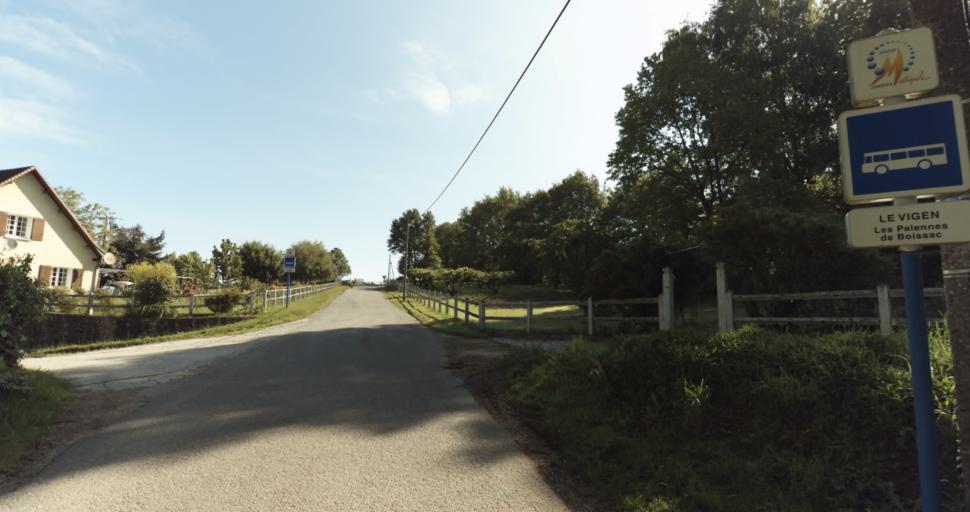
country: FR
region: Limousin
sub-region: Departement de la Haute-Vienne
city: Solignac
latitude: 45.7284
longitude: 1.2566
